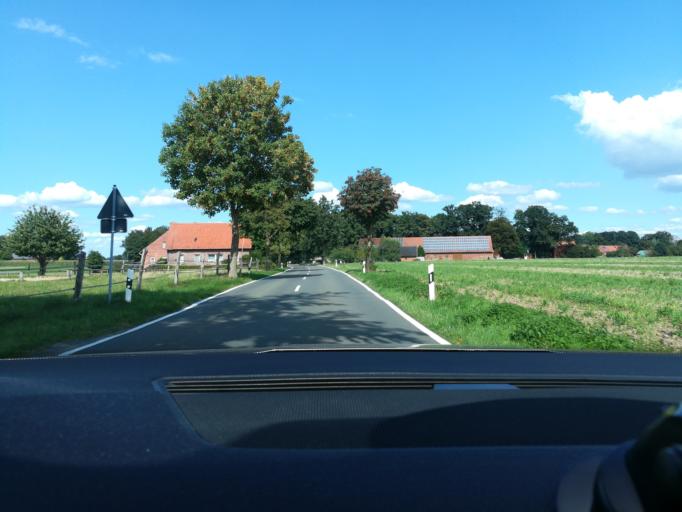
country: DE
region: North Rhine-Westphalia
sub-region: Regierungsbezirk Detmold
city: Hille
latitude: 52.3309
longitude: 8.7823
